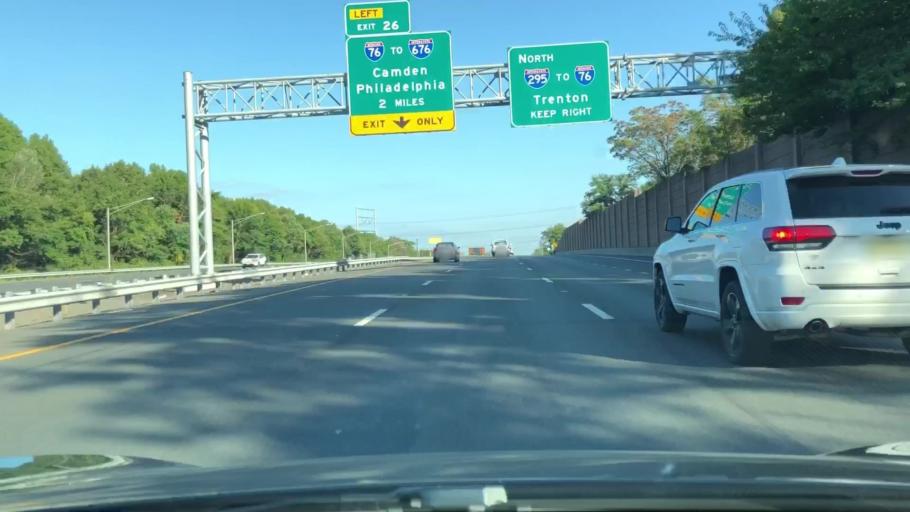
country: US
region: New Jersey
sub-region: Gloucester County
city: Westville
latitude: 39.8606
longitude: -75.1413
